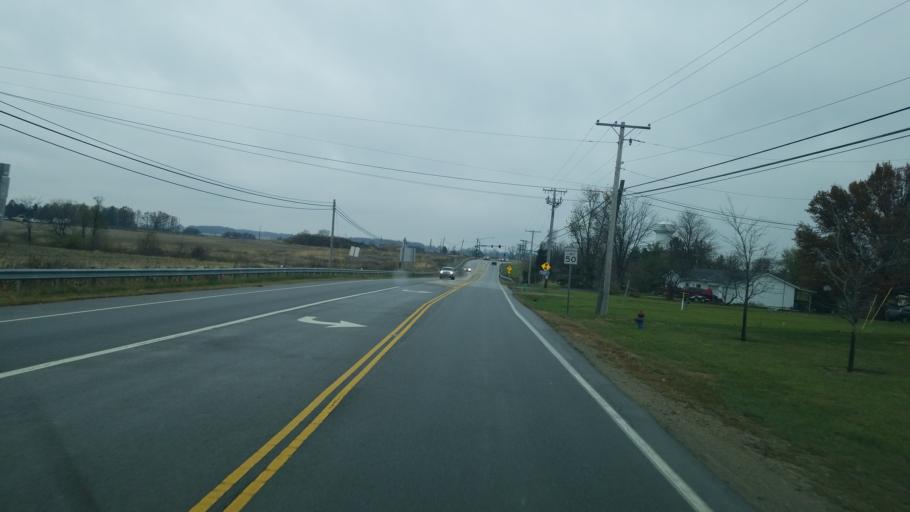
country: US
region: Ohio
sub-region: Union County
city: Marysville
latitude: 40.2595
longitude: -83.3657
